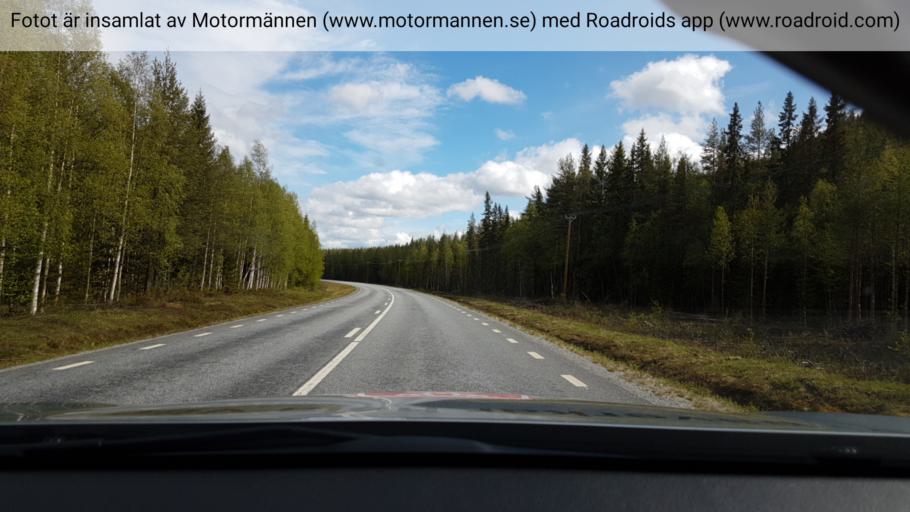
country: SE
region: Vaesterbotten
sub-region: Asele Kommun
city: Insjon
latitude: 64.1692
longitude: 17.8033
